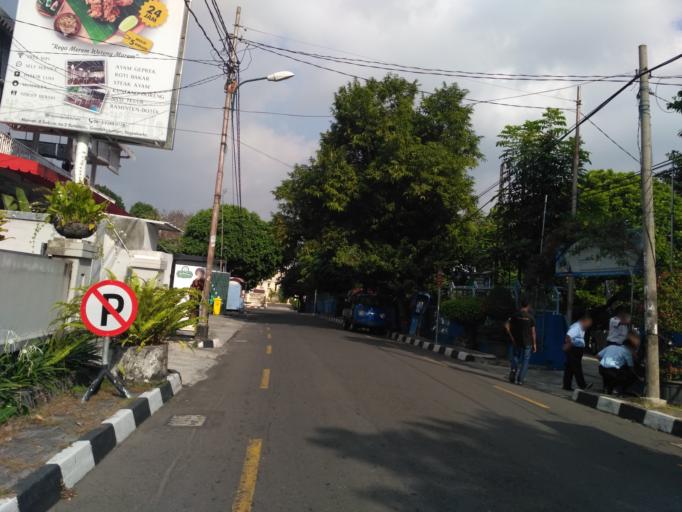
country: ID
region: Daerah Istimewa Yogyakarta
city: Yogyakarta
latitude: -7.7843
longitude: 110.3723
